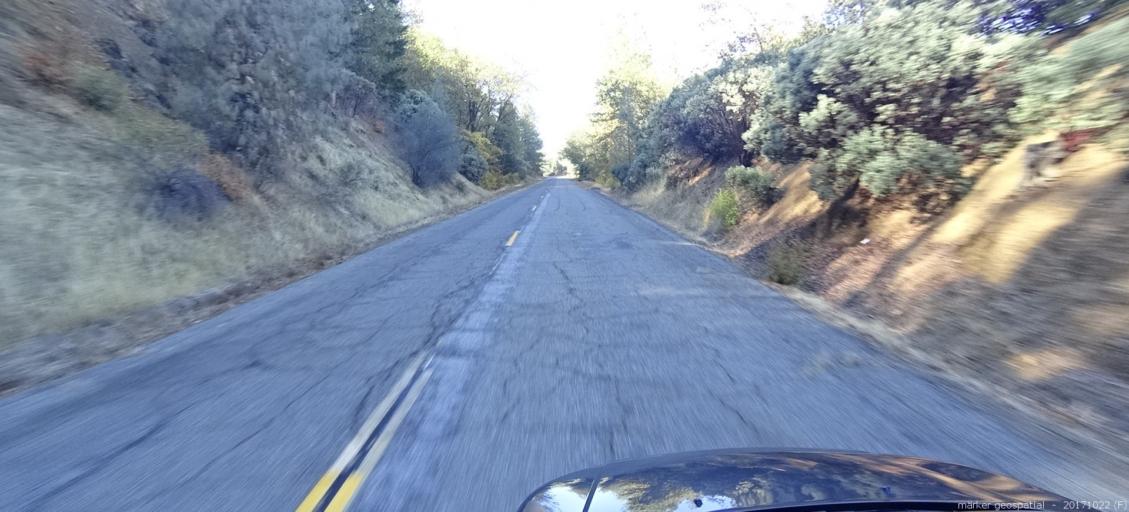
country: US
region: California
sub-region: Shasta County
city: Shasta Lake
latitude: 40.8598
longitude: -122.3556
